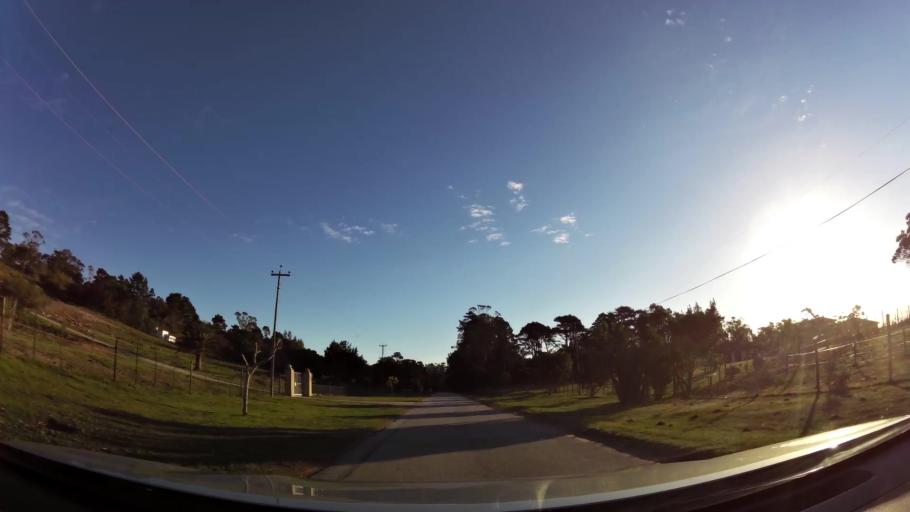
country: ZA
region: Eastern Cape
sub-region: Nelson Mandela Bay Metropolitan Municipality
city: Port Elizabeth
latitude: -33.9876
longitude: 25.4878
